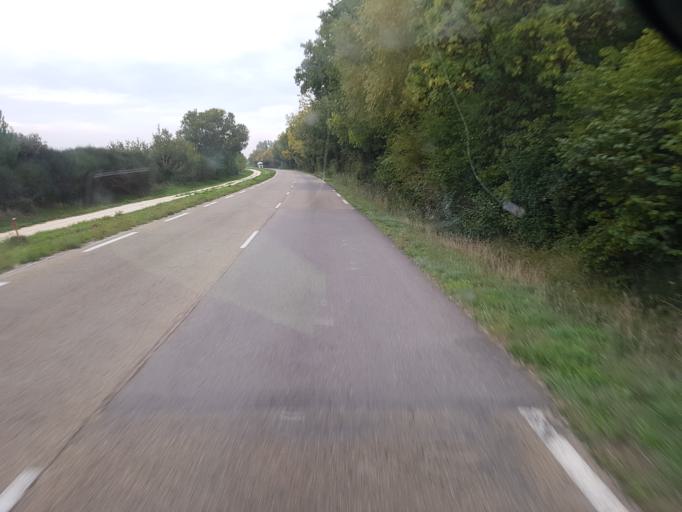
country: FR
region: Provence-Alpes-Cote d'Azur
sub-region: Departement des Bouches-du-Rhone
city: Barbentane
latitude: 43.9221
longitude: 4.7320
